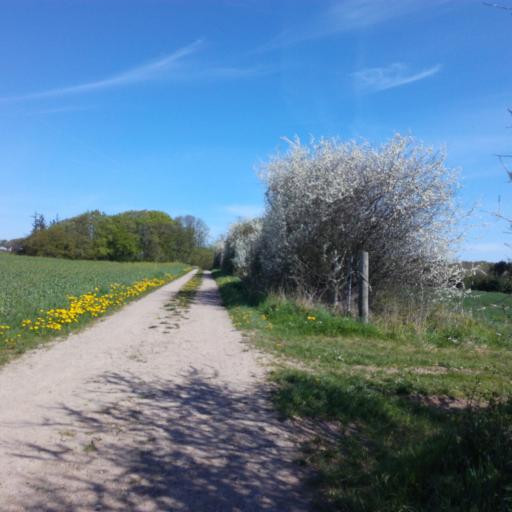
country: DK
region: South Denmark
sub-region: Vejle Kommune
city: Borkop
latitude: 55.6260
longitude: 9.6563
